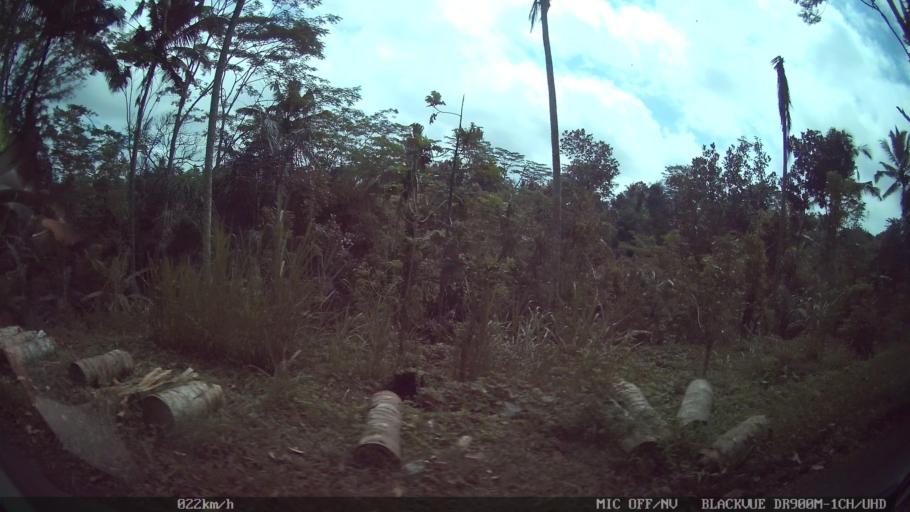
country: ID
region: Bali
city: Banjar Petak
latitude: -8.4456
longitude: 115.3279
